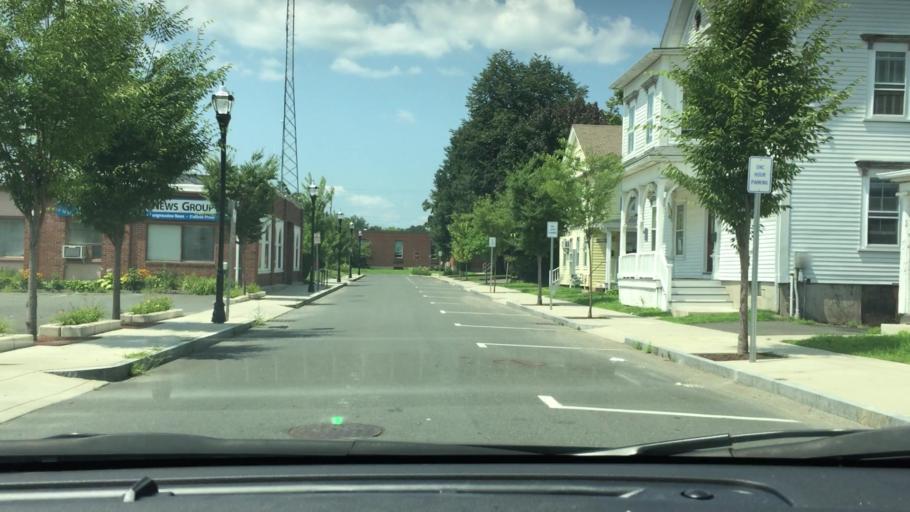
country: US
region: Massachusetts
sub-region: Hampden County
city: Westfield
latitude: 42.1216
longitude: -72.7509
